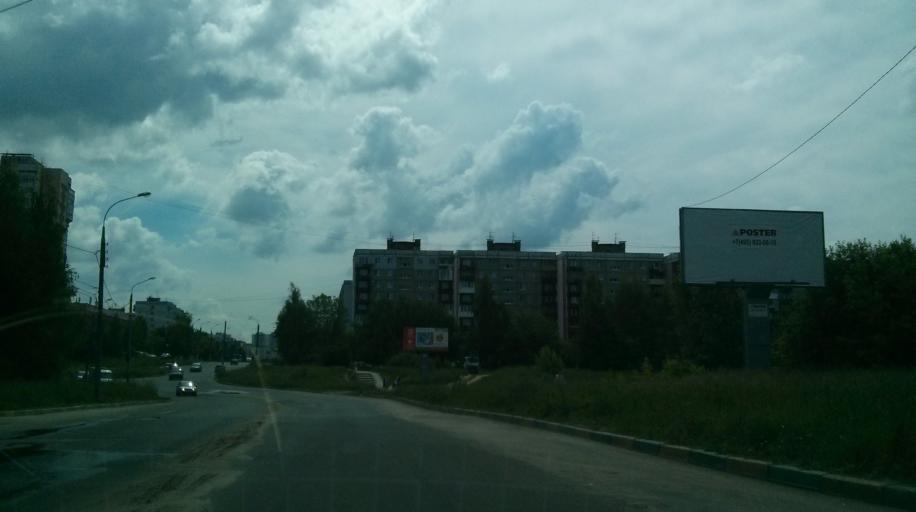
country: RU
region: Nizjnij Novgorod
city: Afonino
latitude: 56.2961
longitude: 44.0678
